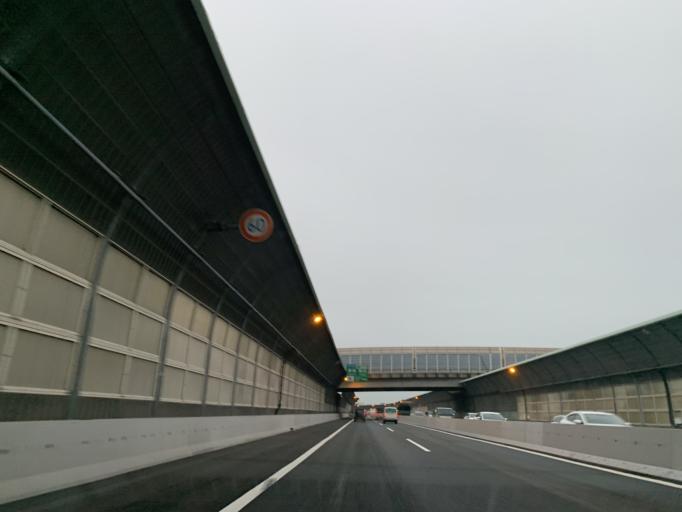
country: JP
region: Chiba
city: Funabashi
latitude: 35.6723
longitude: 140.0202
